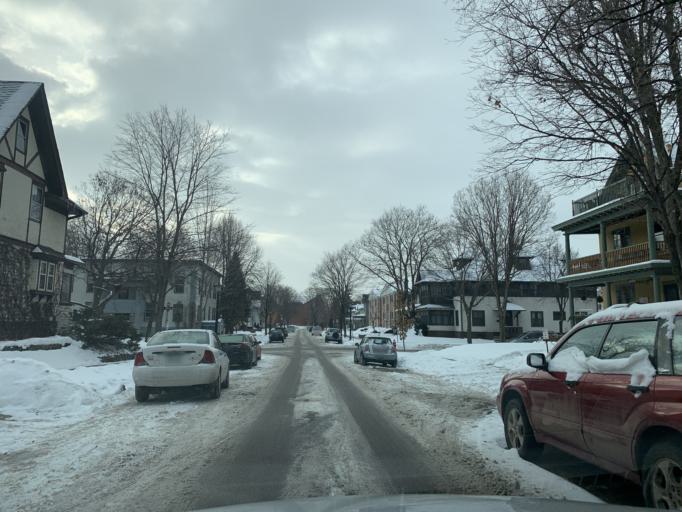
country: US
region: Minnesota
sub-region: Hennepin County
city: Minneapolis
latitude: 44.9577
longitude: -93.2842
